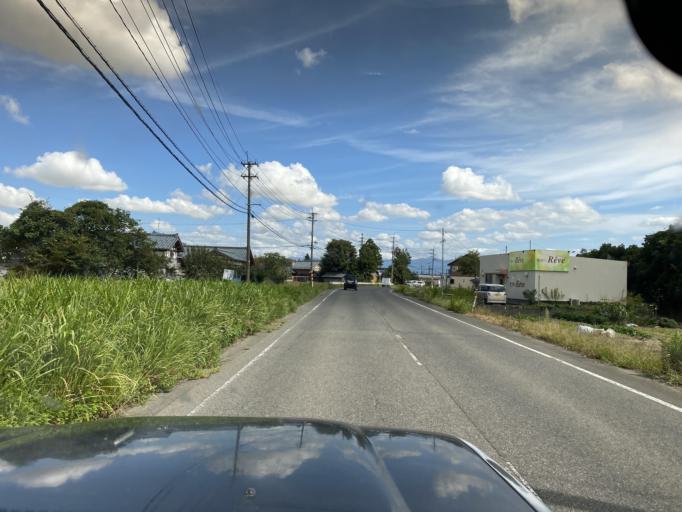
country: JP
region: Niigata
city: Niitsu-honcho
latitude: 37.8150
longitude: 139.1128
